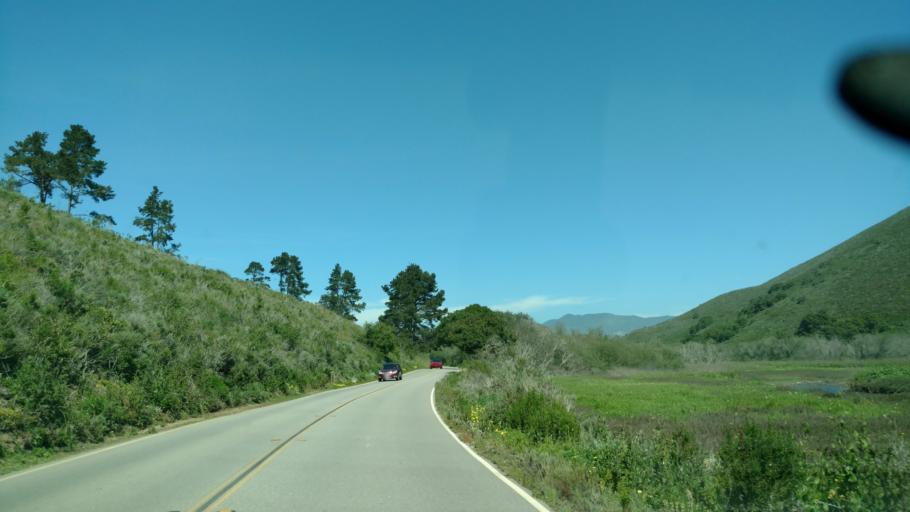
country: US
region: California
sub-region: San Luis Obispo County
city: Morro Bay
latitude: 35.3503
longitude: -120.8328
